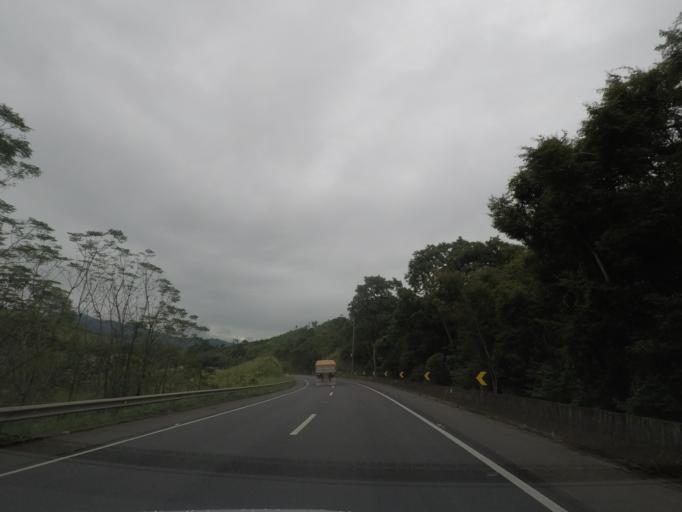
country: BR
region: Sao Paulo
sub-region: Cajati
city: Cajati
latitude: -24.8239
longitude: -48.2090
